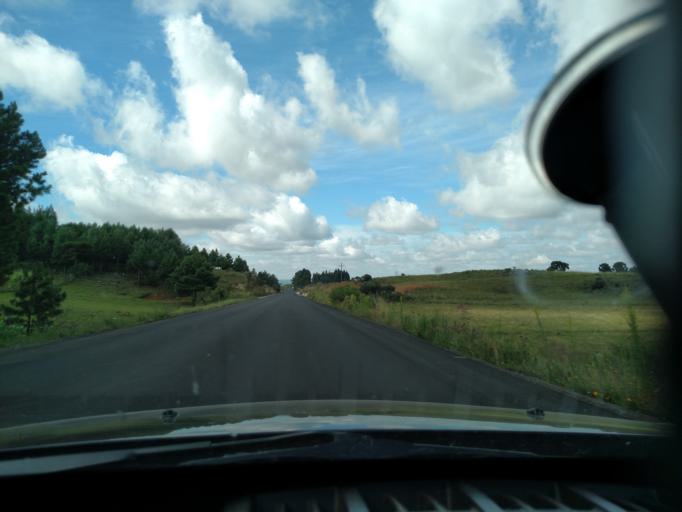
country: BR
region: Santa Catarina
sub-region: Sao Joaquim
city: Sao Joaquim
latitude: -28.0458
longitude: -50.0728
